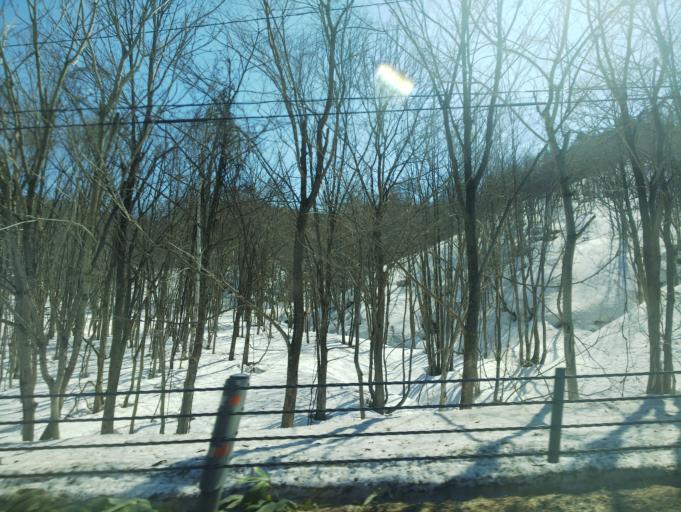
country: JP
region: Hokkaido
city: Nayoro
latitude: 44.7068
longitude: 142.2746
